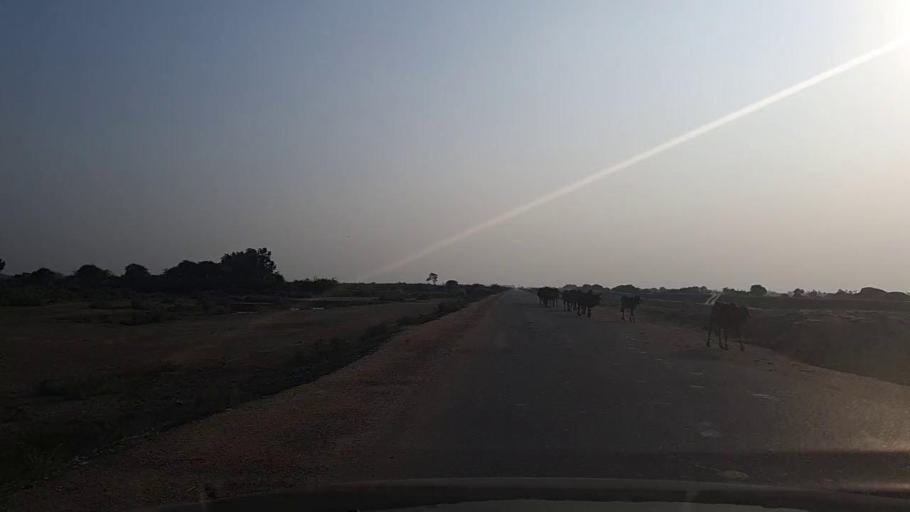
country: PK
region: Sindh
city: Mirpur Sakro
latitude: 24.4854
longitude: 67.8069
